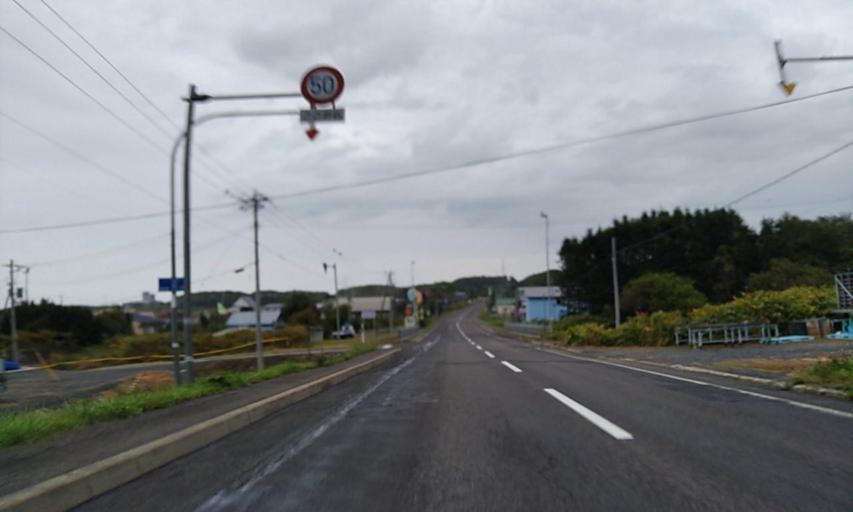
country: JP
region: Hokkaido
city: Mombetsu
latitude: 44.5287
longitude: 143.0429
